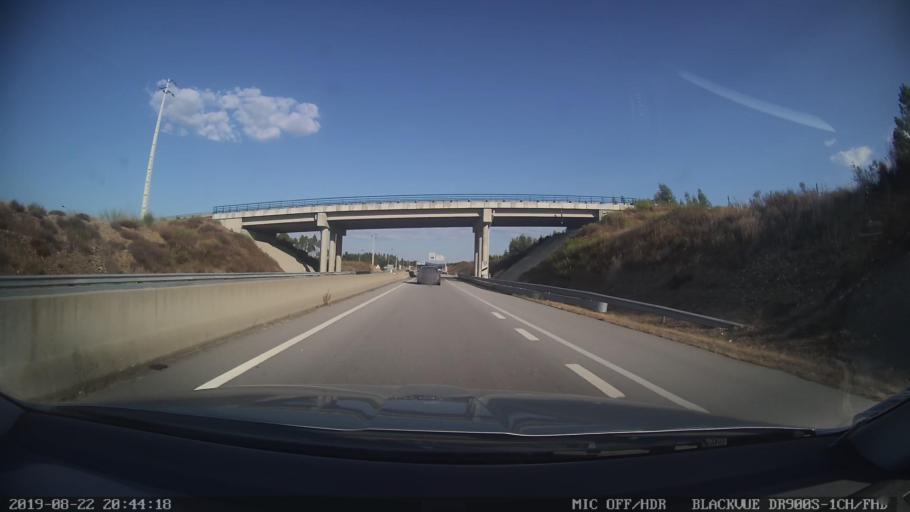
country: PT
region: Castelo Branco
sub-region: Proenca-A-Nova
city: Proenca-a-Nova
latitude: 39.7062
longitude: -7.8488
